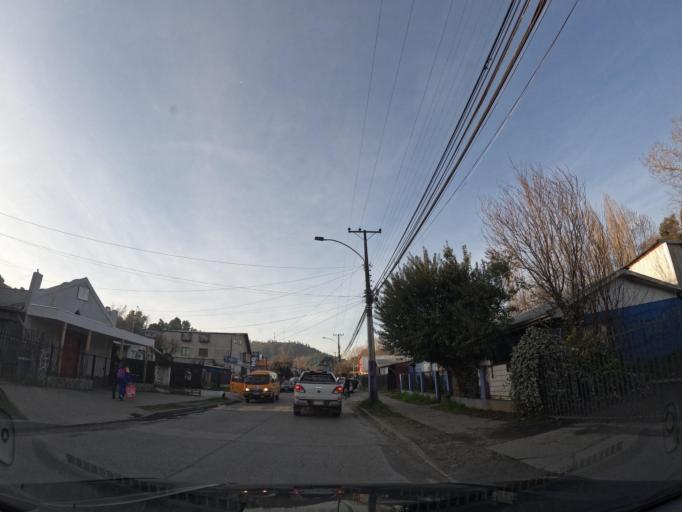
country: CL
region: Biobio
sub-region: Provincia de Concepcion
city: Concepcion
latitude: -36.8373
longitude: -73.0039
